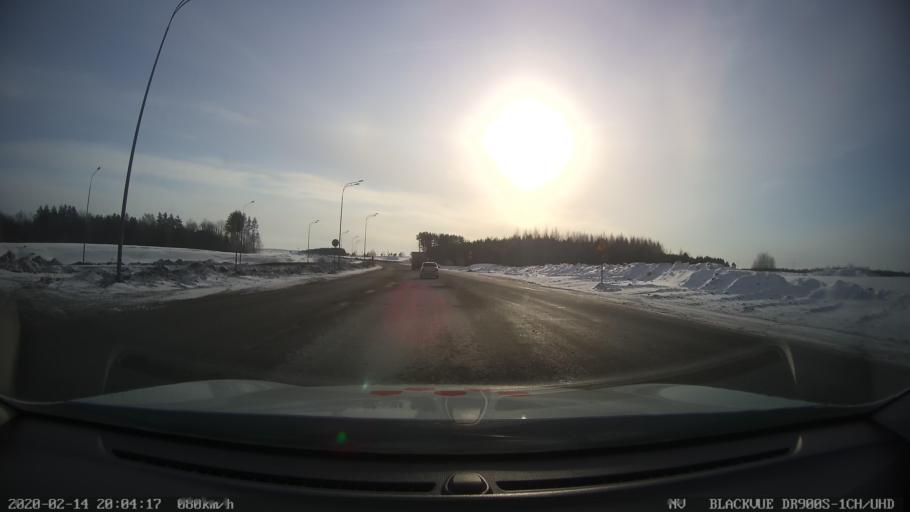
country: RU
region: Tatarstan
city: Sviyazhsk
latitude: 55.7360
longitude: 48.7872
